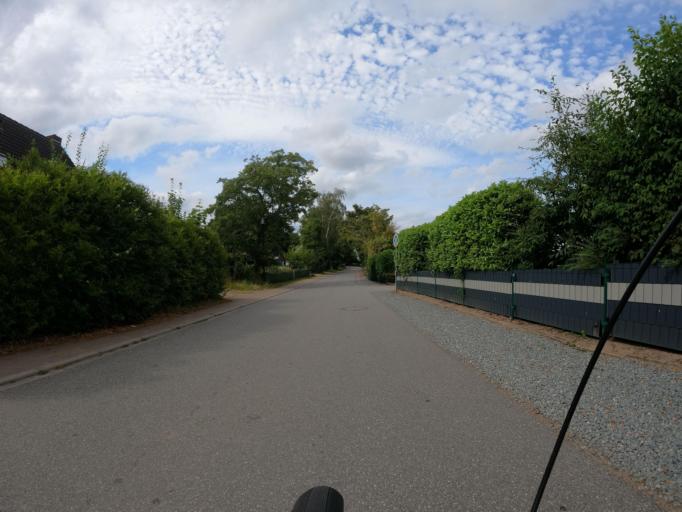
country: DE
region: Schleswig-Holstein
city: Steinberg
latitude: 54.7553
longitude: 9.7853
